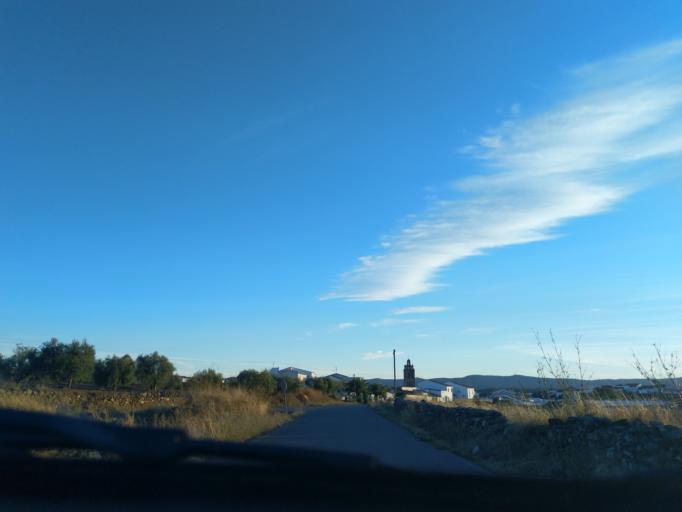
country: ES
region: Extremadura
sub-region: Provincia de Badajoz
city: Valverde de Llerena
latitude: 38.2176
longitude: -5.8214
